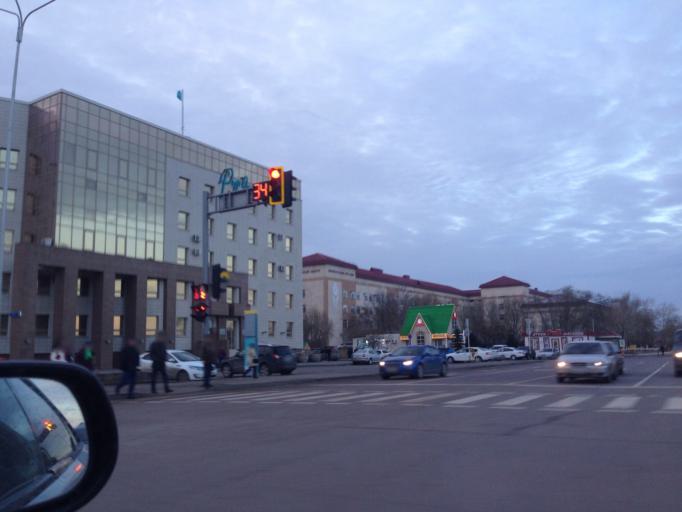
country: KZ
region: Astana Qalasy
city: Astana
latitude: 51.1512
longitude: 71.4562
